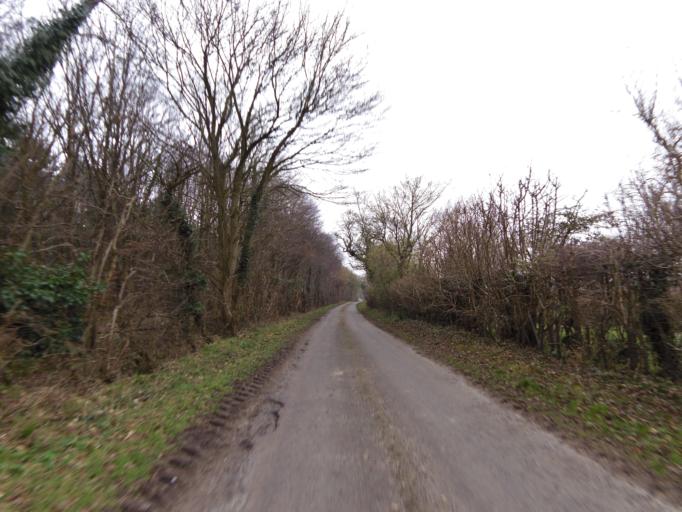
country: GB
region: England
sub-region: Suffolk
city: Cookley
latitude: 52.2574
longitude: 1.4185
